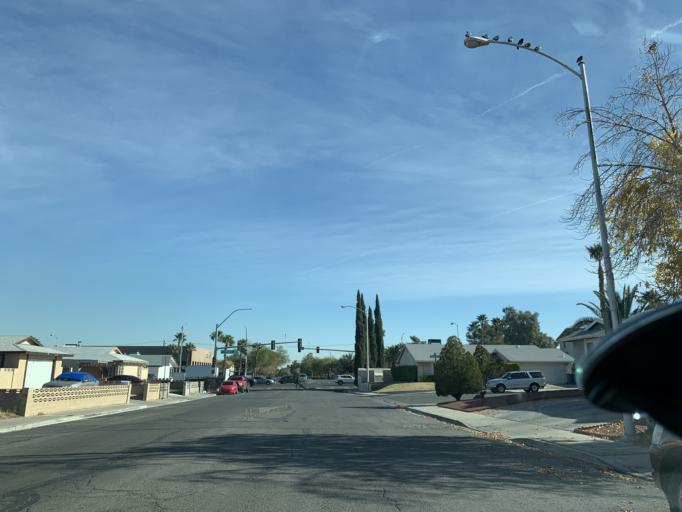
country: US
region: Nevada
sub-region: Clark County
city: Spring Valley
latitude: 36.0963
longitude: -115.2261
